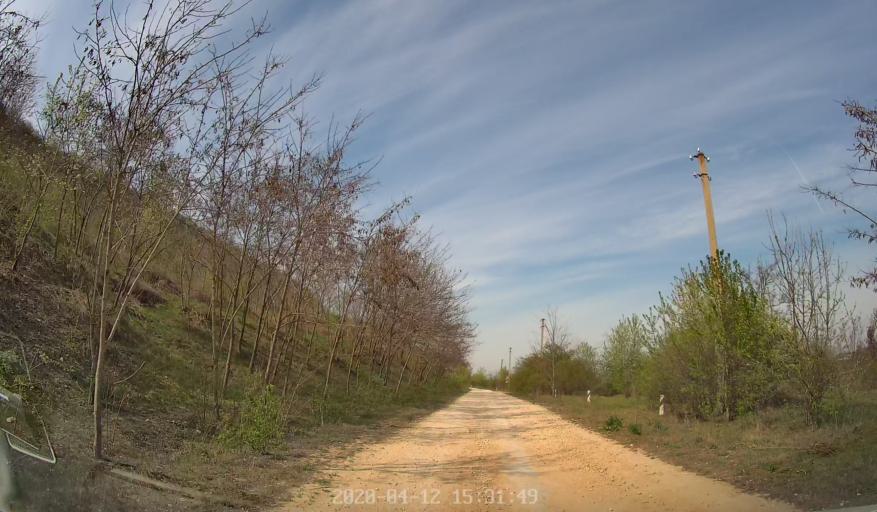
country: MD
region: Telenesti
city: Cocieri
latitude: 47.3245
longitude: 29.0739
